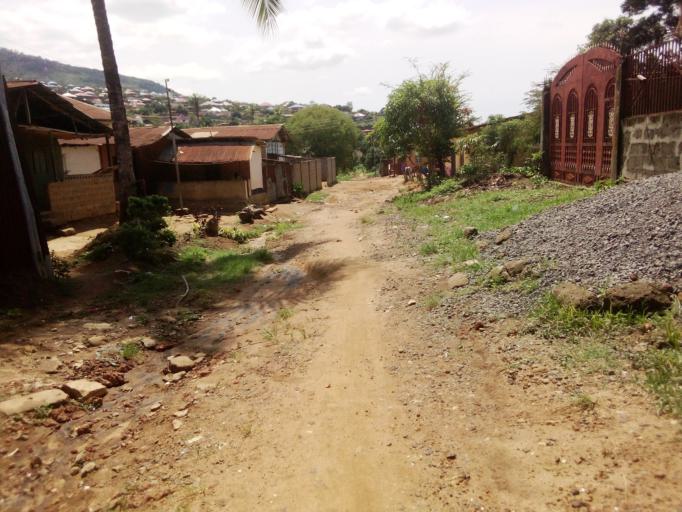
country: SL
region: Western Area
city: Waterloo
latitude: 8.3411
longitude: -13.0718
